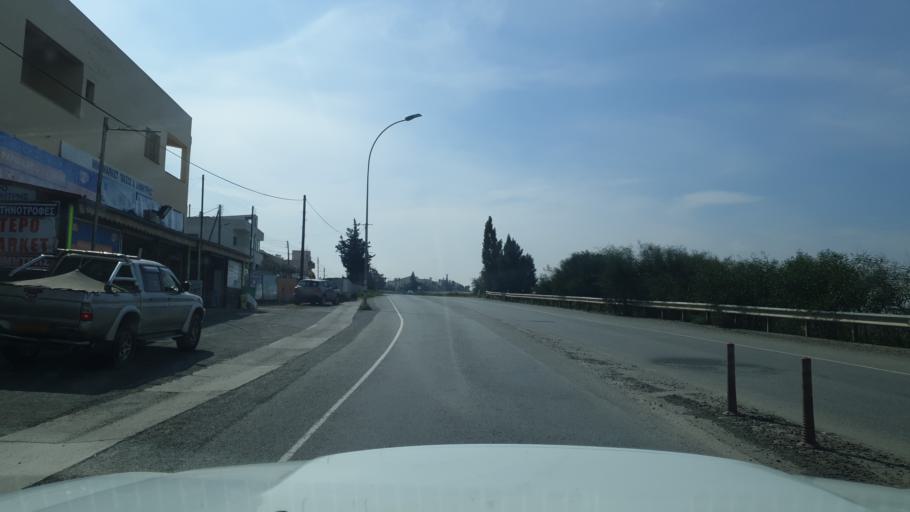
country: CY
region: Lefkosia
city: Kato Deftera
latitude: 35.1233
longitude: 33.2903
